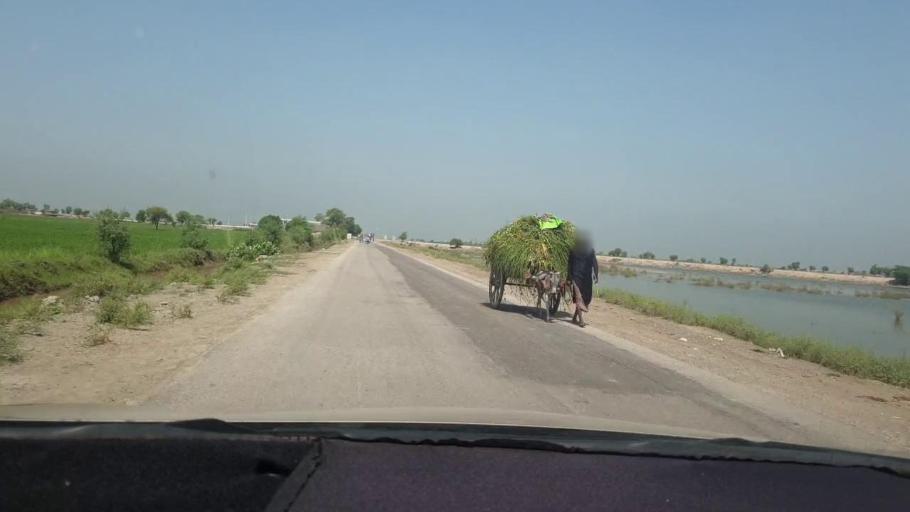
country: PK
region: Sindh
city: Shahdadkot
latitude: 27.8447
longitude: 68.0022
